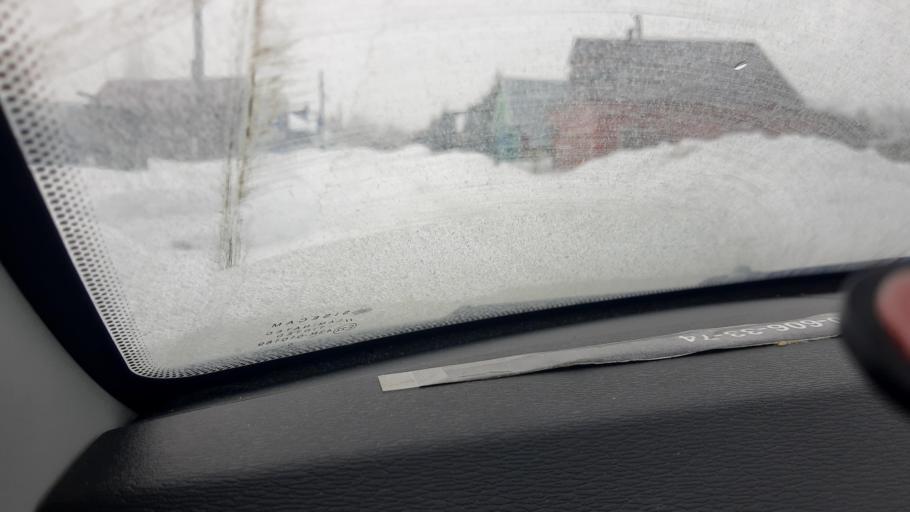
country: RU
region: Nizjnij Novgorod
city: Sitniki
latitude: 56.5301
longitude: 44.0610
